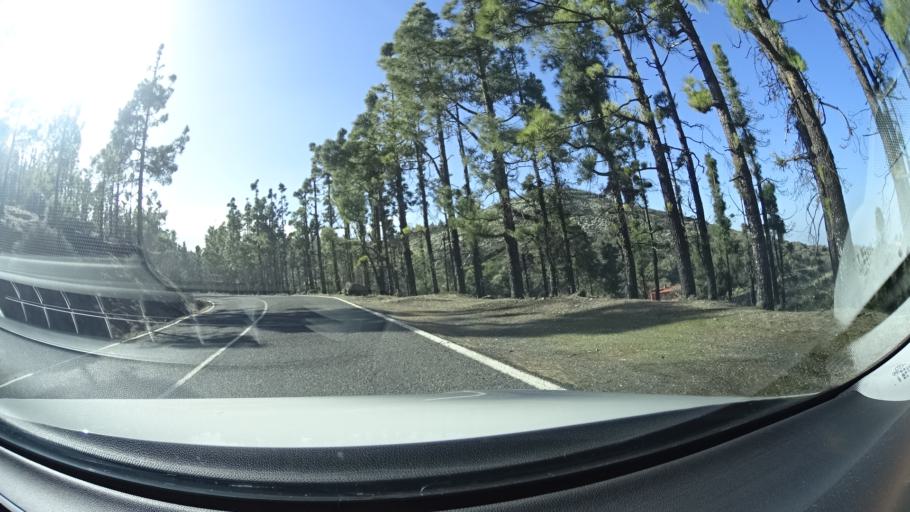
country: ES
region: Canary Islands
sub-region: Provincia de Las Palmas
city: San Bartolome
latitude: 27.9651
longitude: -15.5550
